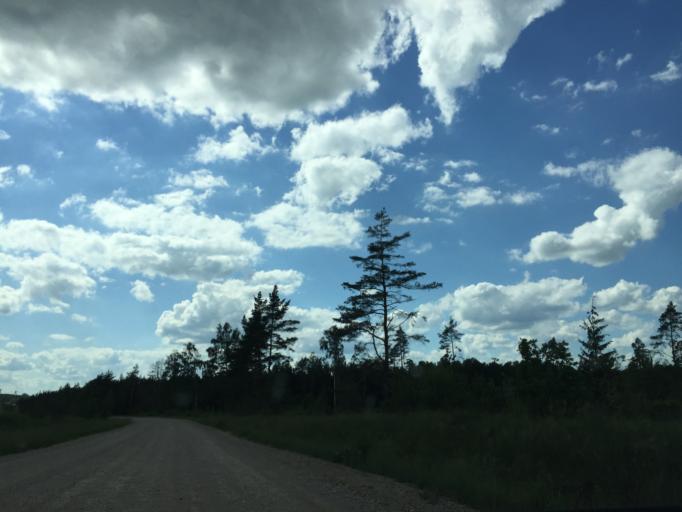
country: LV
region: Tukuma Rajons
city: Tukums
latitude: 56.9110
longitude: 23.1750
